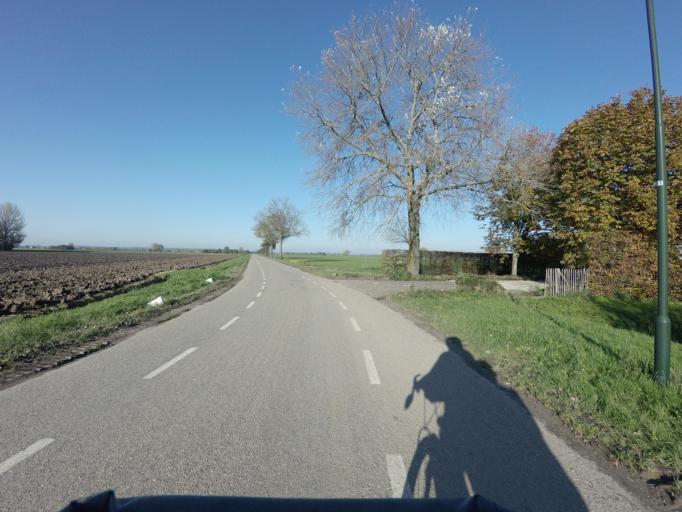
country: NL
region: North Brabant
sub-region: Gemeente Waalwijk
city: Waalwijk
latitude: 51.7370
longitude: 5.0664
